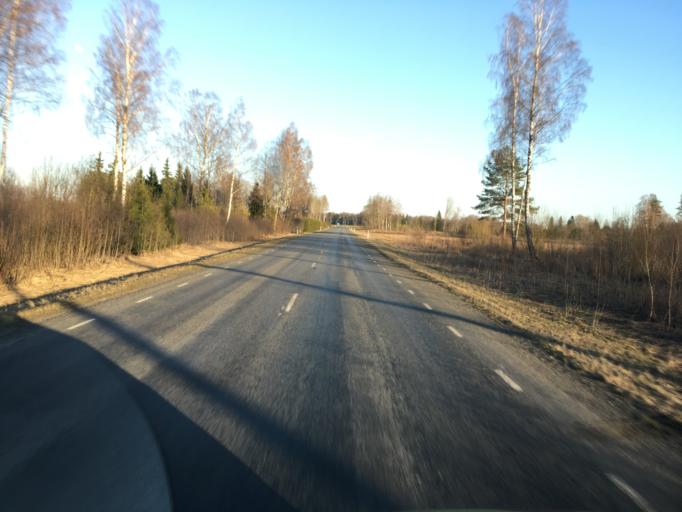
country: EE
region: Raplamaa
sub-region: Kehtna vald
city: Kehtna
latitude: 59.0614
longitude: 24.9360
